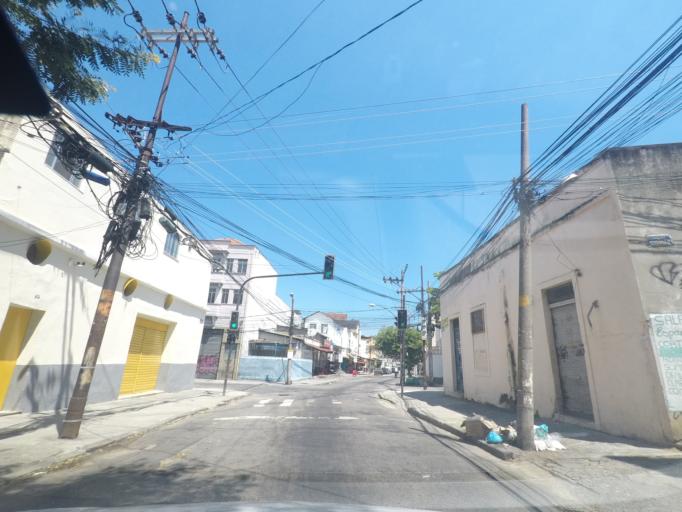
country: BR
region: Rio de Janeiro
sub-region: Rio De Janeiro
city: Rio de Janeiro
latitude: -22.8946
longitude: -43.2218
